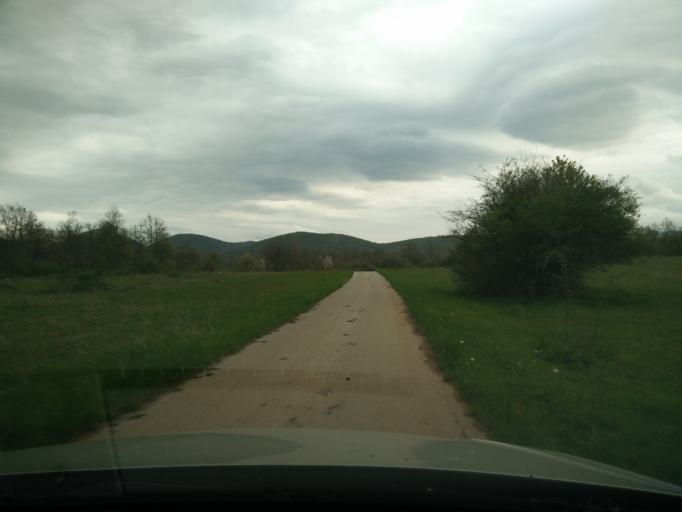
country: HR
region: Zadarska
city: Gracac
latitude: 44.3998
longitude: 15.6869
